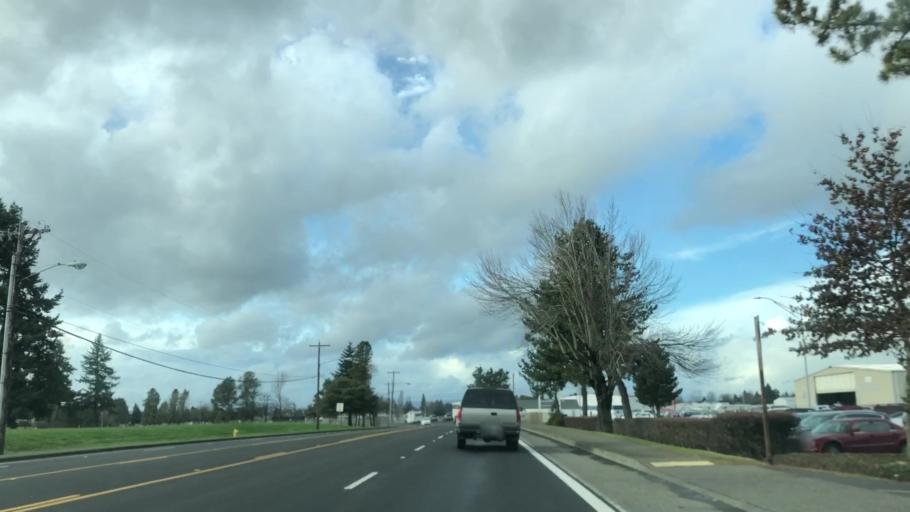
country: US
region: Oregon
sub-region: Washington County
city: Hillsboro
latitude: 45.5323
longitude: -122.9480
